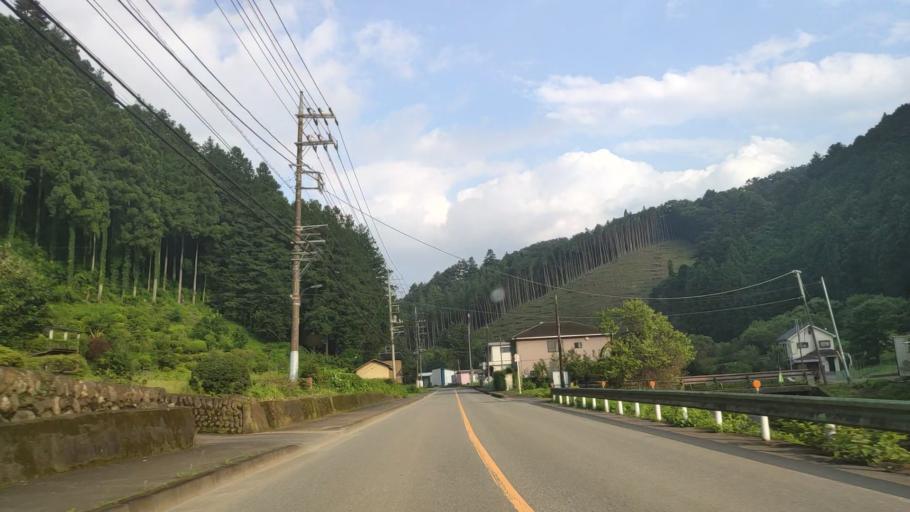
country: JP
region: Tokyo
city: Ome
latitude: 35.8291
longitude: 139.2397
